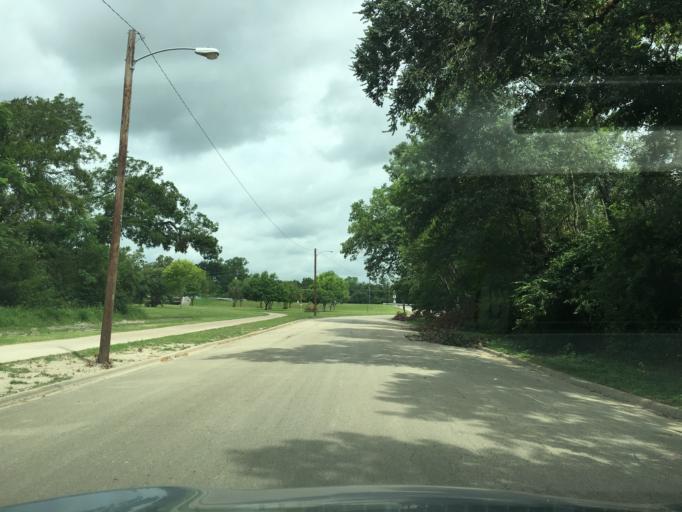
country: US
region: Texas
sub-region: Dallas County
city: University Park
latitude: 32.8795
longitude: -96.7469
